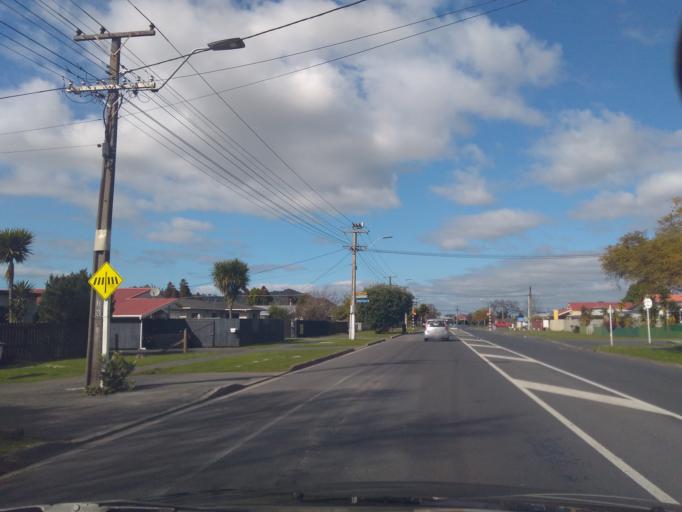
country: NZ
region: Northland
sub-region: Whangarei
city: Whangarei
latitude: -35.6900
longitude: 174.3271
